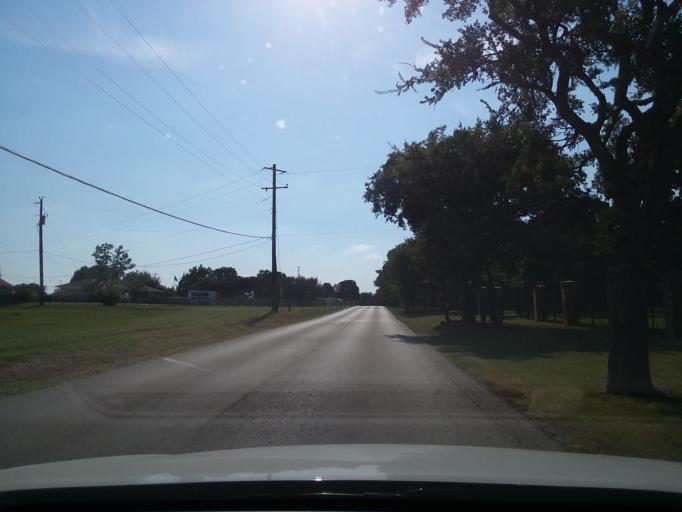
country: US
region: Texas
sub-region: Denton County
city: Double Oak
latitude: 33.0587
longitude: -97.1250
